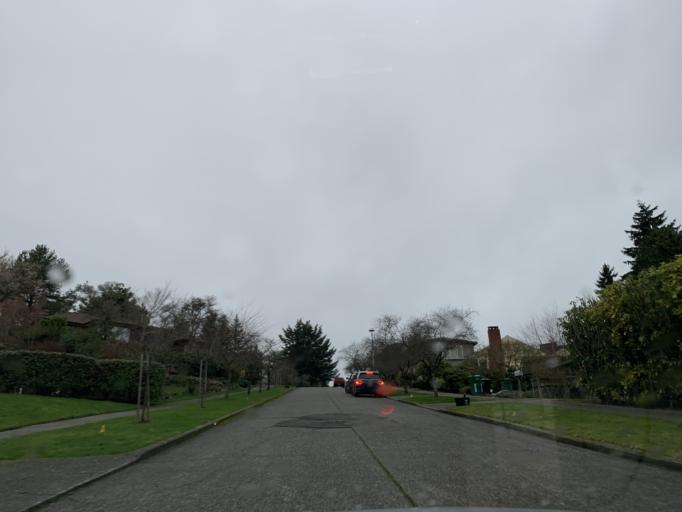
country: US
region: Washington
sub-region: King County
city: Yarrow Point
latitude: 47.6676
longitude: -122.2719
